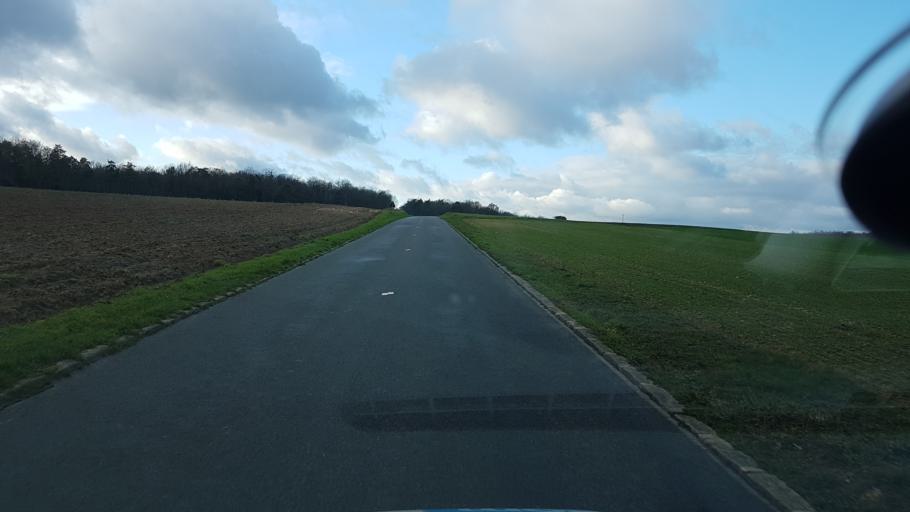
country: FR
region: Ile-de-France
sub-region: Departement de Seine-et-Marne
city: Montigny-sur-Loing
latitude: 48.2753
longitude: 2.7903
